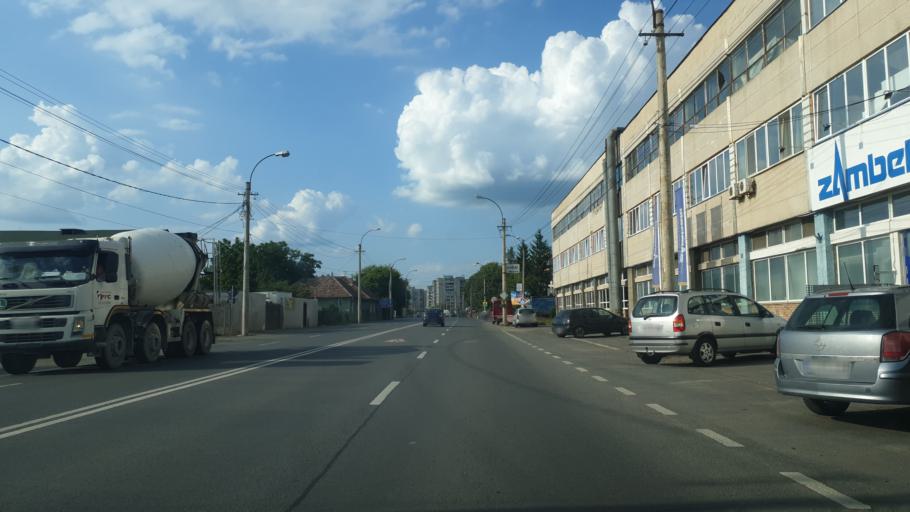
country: RO
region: Covasna
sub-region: Municipiul Sfantu Gheorghe
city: Sfantu-Gheorghe
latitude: 45.8552
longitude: 25.8068
